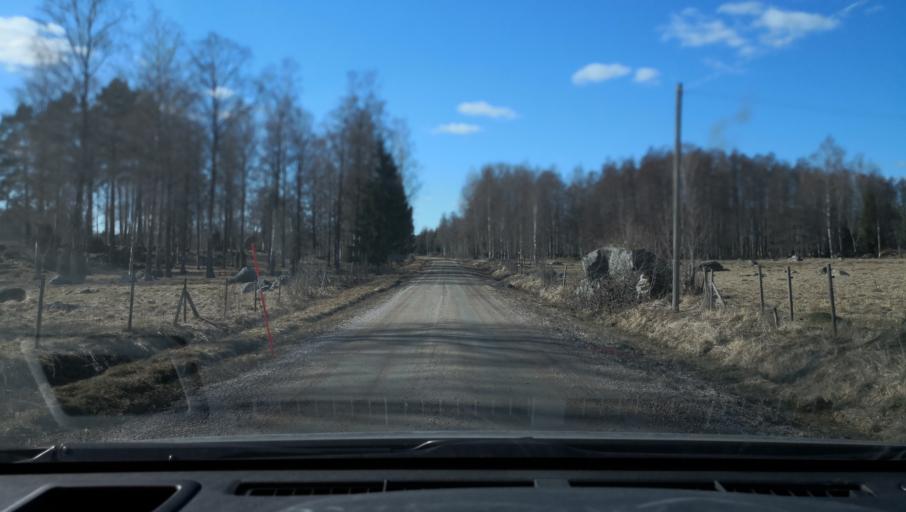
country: SE
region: Vaestmanland
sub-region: Sala Kommun
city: Sala
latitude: 60.1130
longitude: 16.6848
